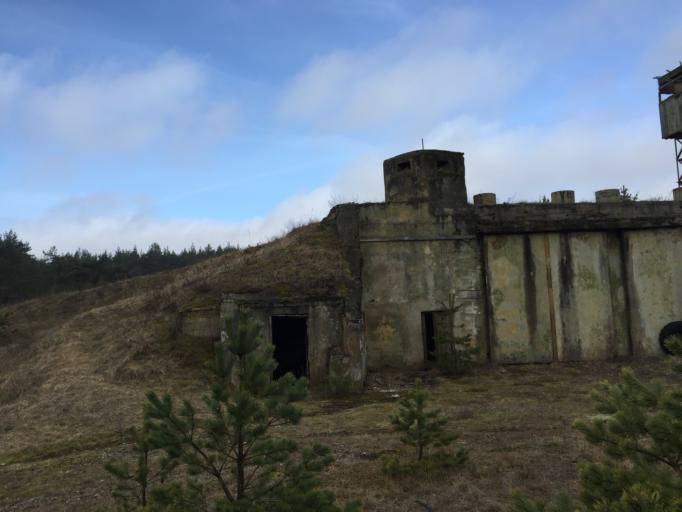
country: EE
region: Saare
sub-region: Kuressaare linn
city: Kuressaare
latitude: 58.1860
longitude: 22.2538
